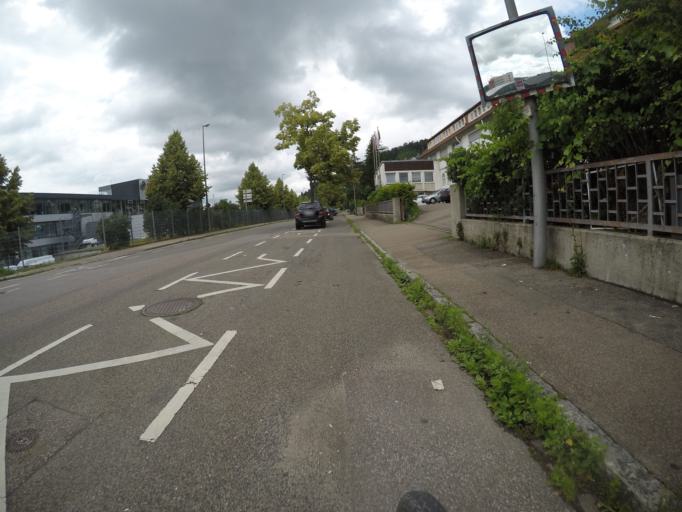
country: DE
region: Baden-Wuerttemberg
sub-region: Regierungsbezirk Stuttgart
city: Plochingen
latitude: 48.7187
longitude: 9.4093
